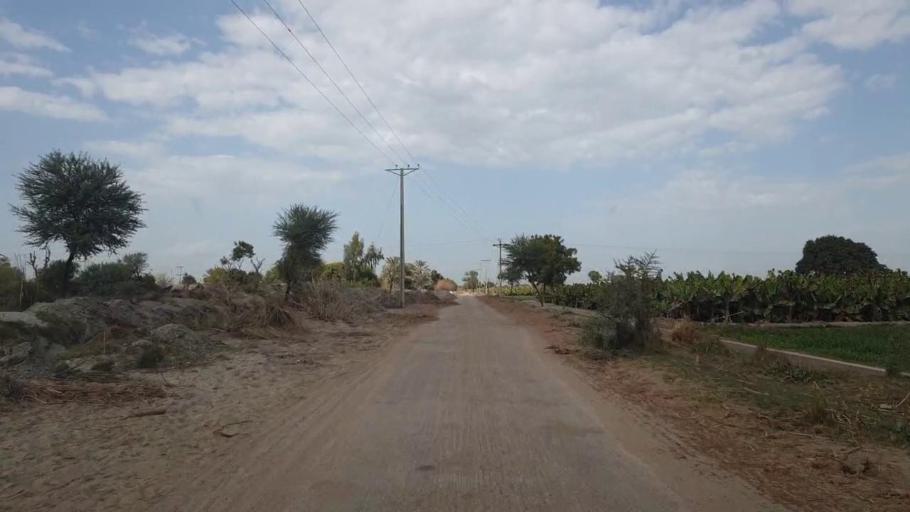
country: PK
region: Sindh
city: Shahdadpur
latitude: 25.9667
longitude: 68.4766
